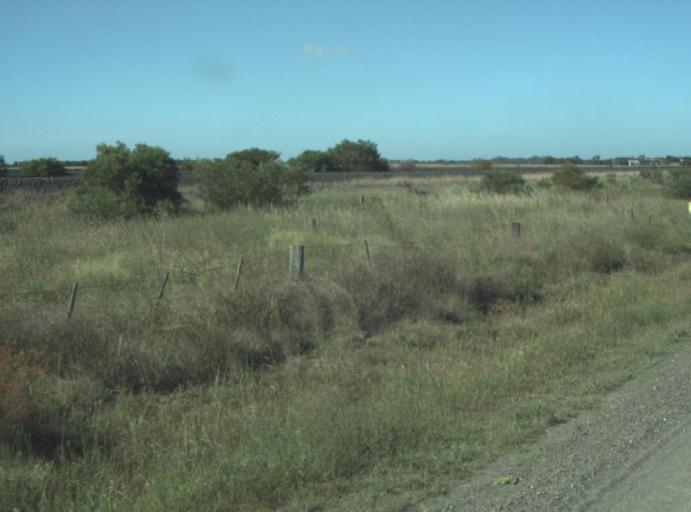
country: AU
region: Victoria
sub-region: Wyndham
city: Little River
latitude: -37.9898
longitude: 144.4563
